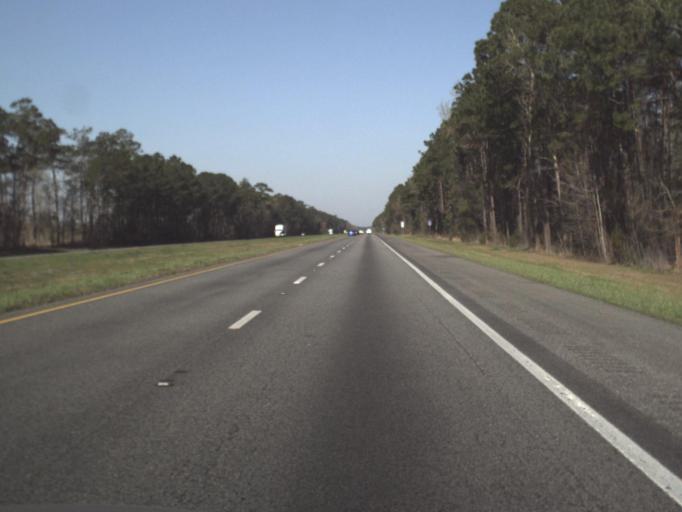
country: US
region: Florida
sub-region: Jefferson County
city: Monticello
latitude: 30.4581
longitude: -83.7713
